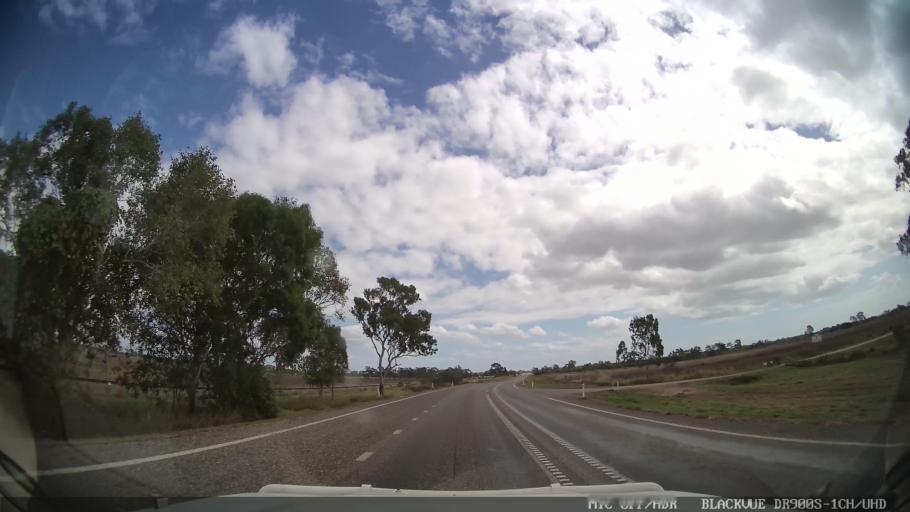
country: AU
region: Queensland
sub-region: Burdekin
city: Home Hill
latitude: -19.9080
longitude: 147.7769
